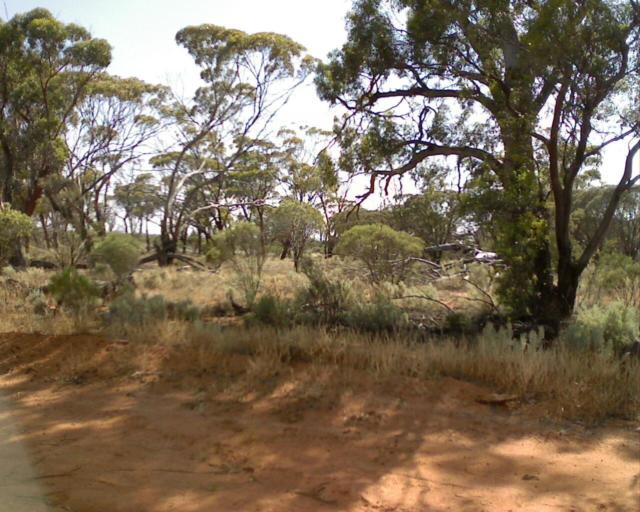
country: AU
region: Western Australia
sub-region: Merredin
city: Merredin
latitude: -30.9618
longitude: 118.8911
